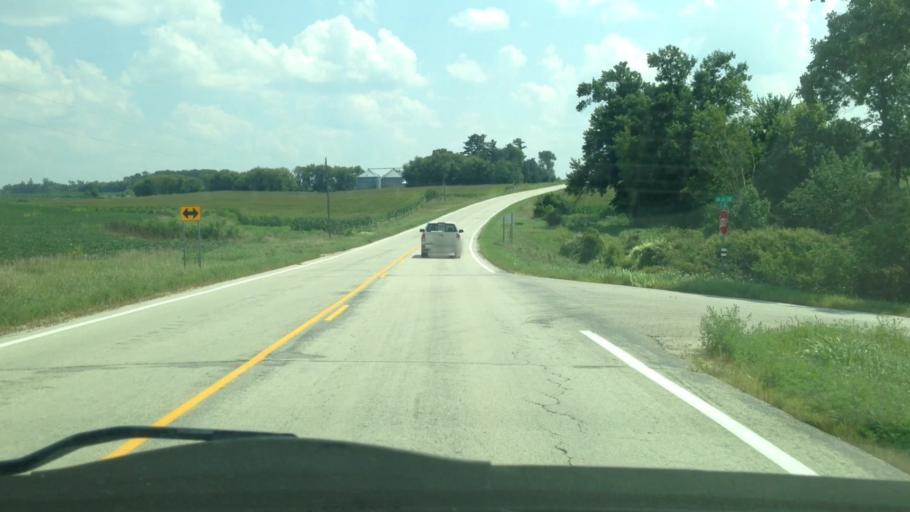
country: US
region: Minnesota
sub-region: Olmsted County
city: Stewartville
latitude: 43.8810
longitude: -92.4064
